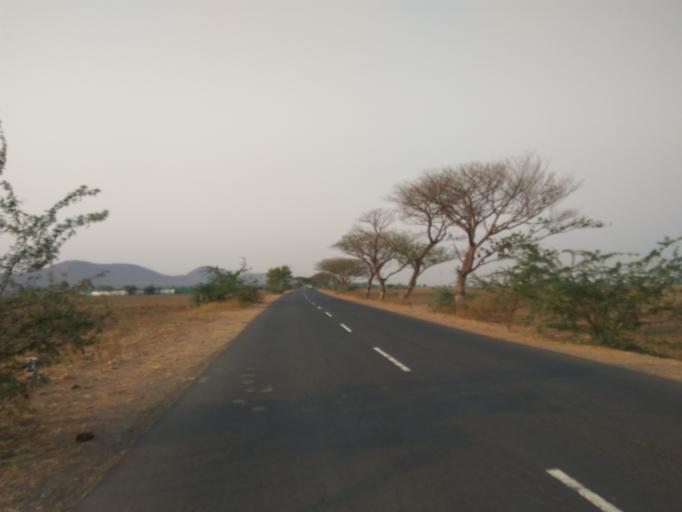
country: IN
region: Andhra Pradesh
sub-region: Prakasam
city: Cumbum
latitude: 15.6289
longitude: 79.1366
